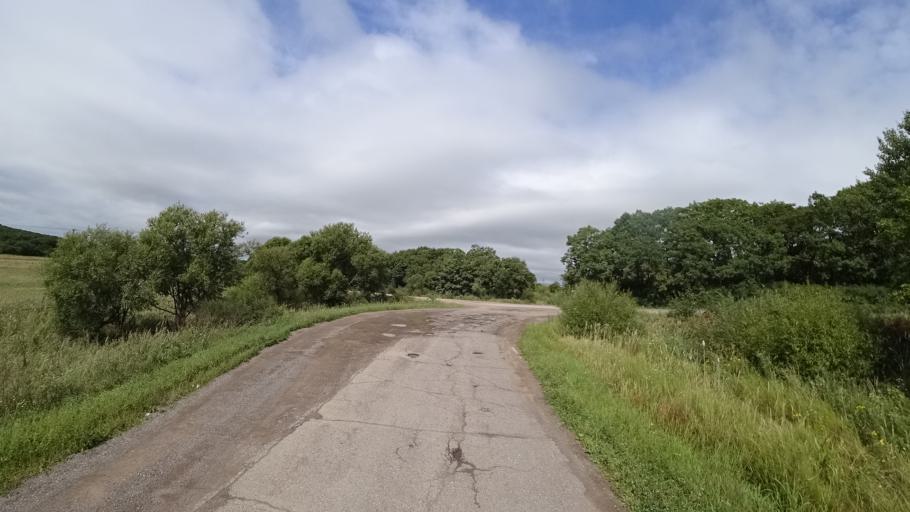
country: RU
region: Primorskiy
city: Lyalichi
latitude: 44.1521
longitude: 132.3913
